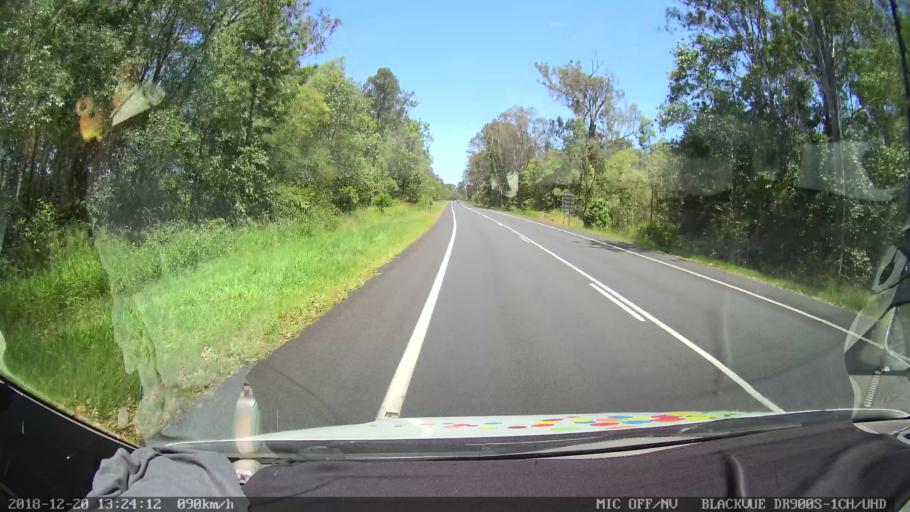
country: AU
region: New South Wales
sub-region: Richmond Valley
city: Casino
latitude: -29.1142
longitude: 153.0003
